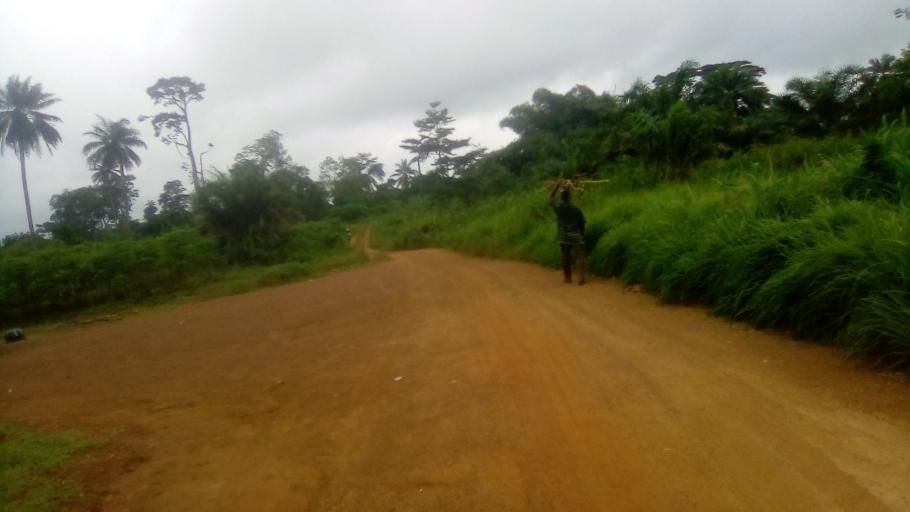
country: SL
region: Eastern Province
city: Kailahun
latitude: 8.3048
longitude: -10.5595
